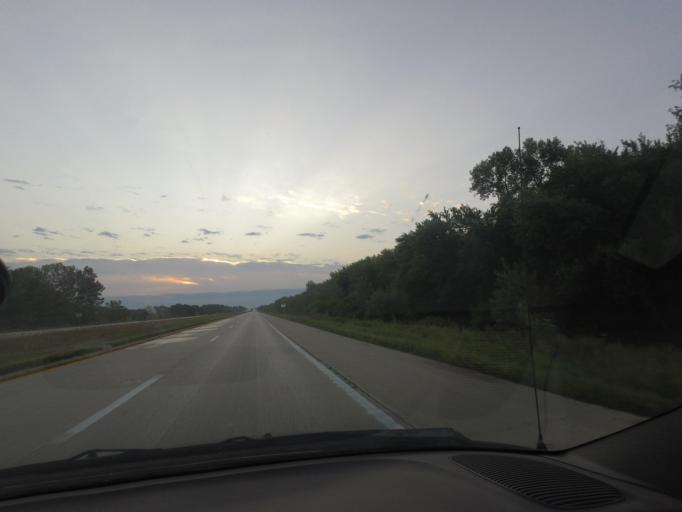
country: US
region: Missouri
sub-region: Macon County
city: Macon
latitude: 39.7532
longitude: -92.4130
